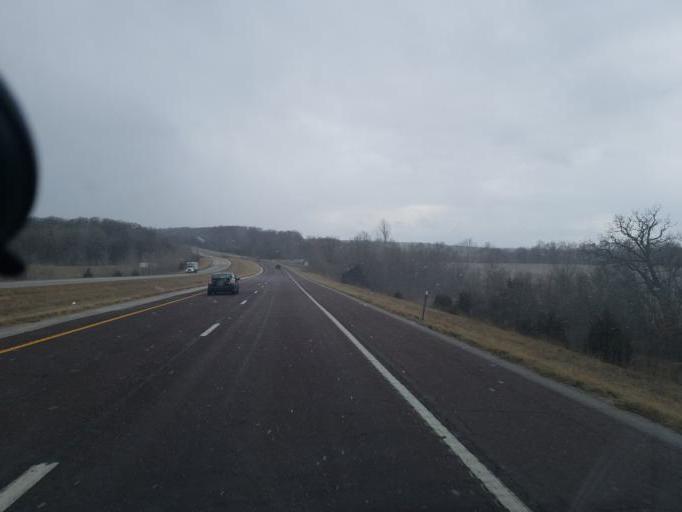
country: US
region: Missouri
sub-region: Boone County
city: Hallsville
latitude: 39.1302
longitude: -92.3331
